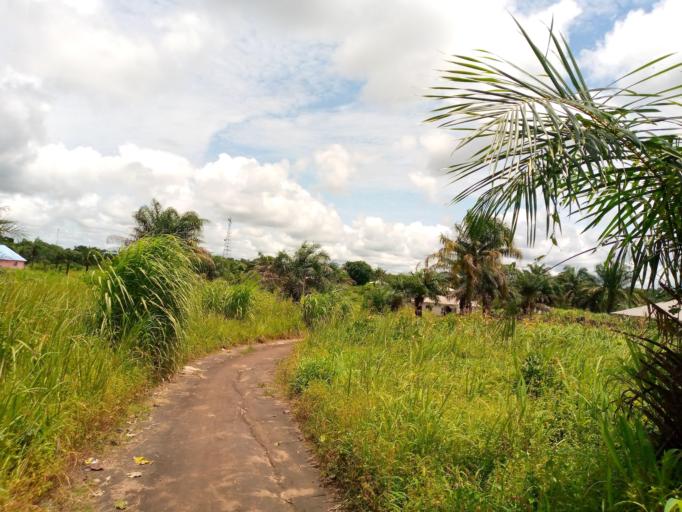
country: SL
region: Northern Province
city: Magburaka
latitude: 8.7200
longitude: -11.9250
